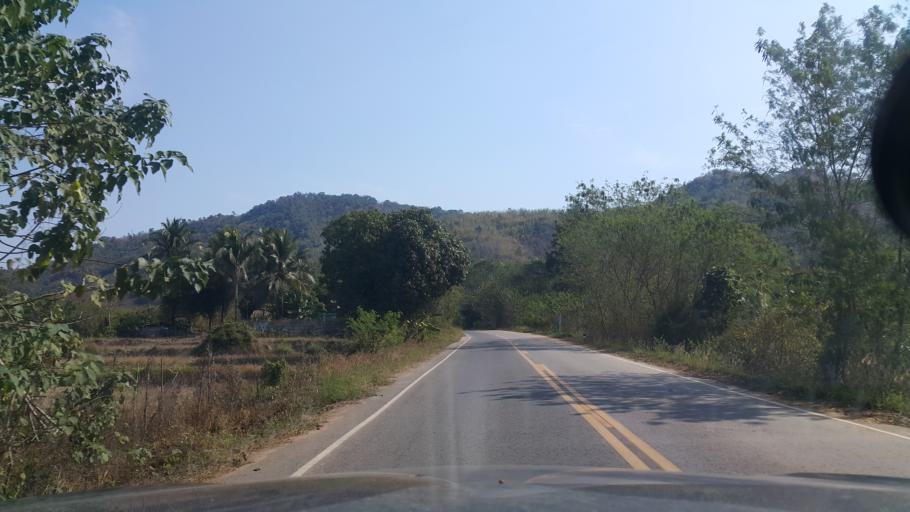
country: TH
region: Loei
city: Pak Chom
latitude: 18.1003
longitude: 102.0348
